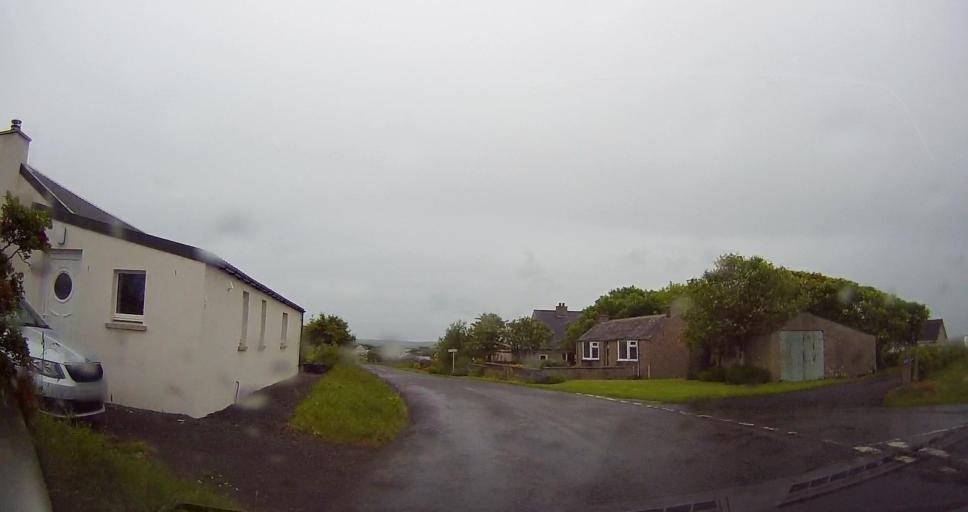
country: GB
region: Scotland
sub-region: Orkney Islands
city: Stromness
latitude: 59.0734
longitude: -3.2207
